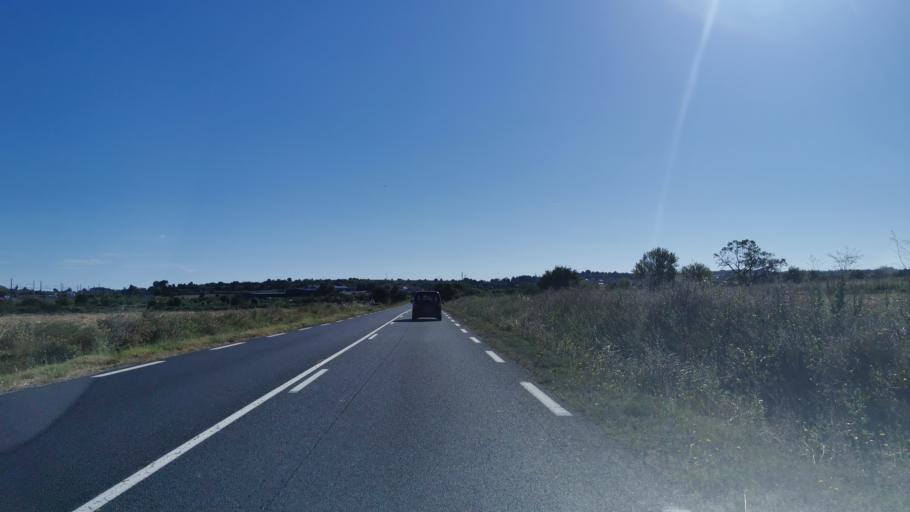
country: FR
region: Languedoc-Roussillon
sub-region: Departement de l'Herault
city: Nissan-lez-Enserune
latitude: 43.2861
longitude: 3.1076
